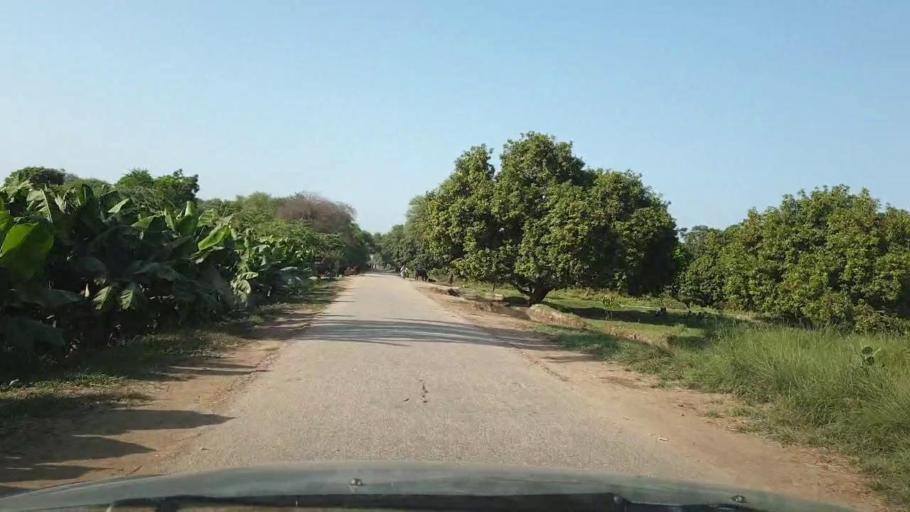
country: PK
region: Sindh
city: Tando Ghulam Ali
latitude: 25.1322
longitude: 68.8949
